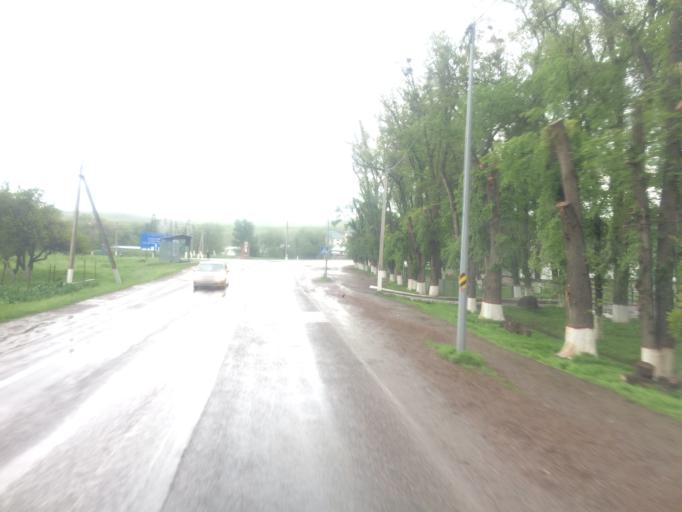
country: KZ
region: Zhambyl
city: Georgiyevka
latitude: 43.2339
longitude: 74.7599
